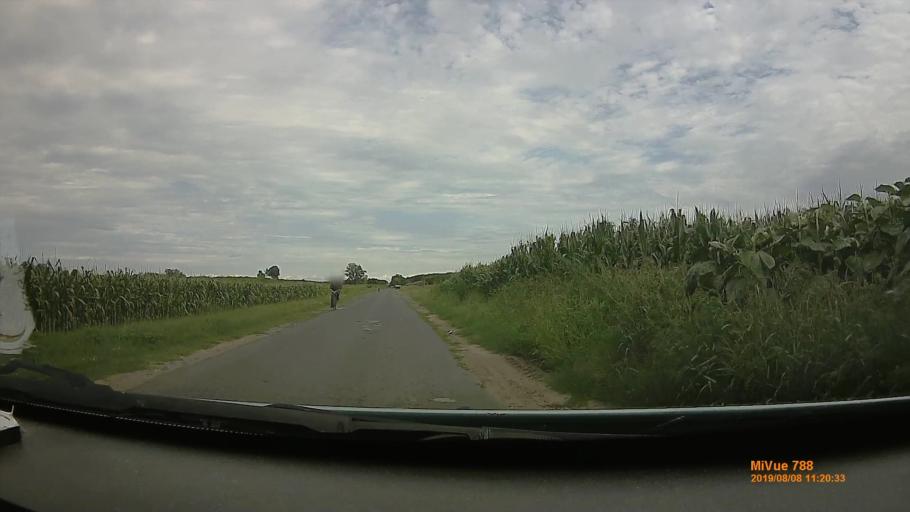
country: HU
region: Szabolcs-Szatmar-Bereg
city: Balkany
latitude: 47.7517
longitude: 21.8438
